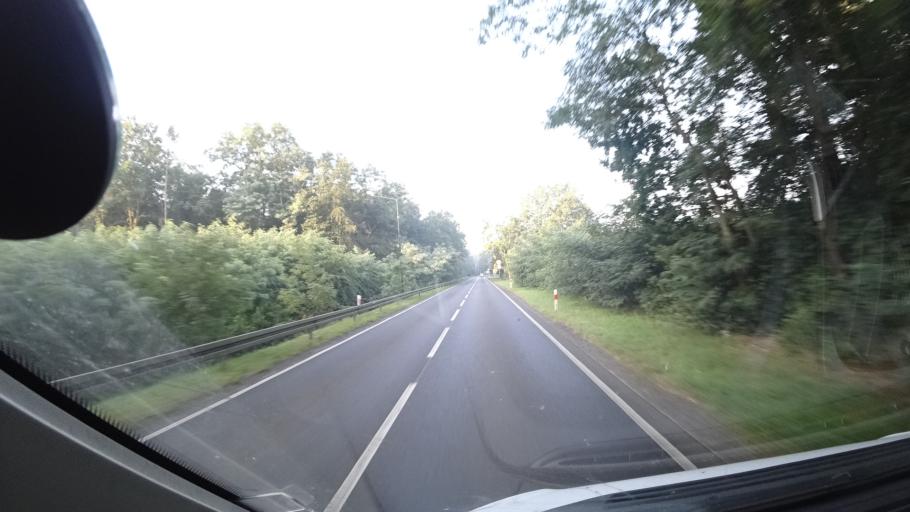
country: PL
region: Opole Voivodeship
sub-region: Powiat kedzierzynsko-kozielski
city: Slawiecice
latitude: 50.3700
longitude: 18.3165
